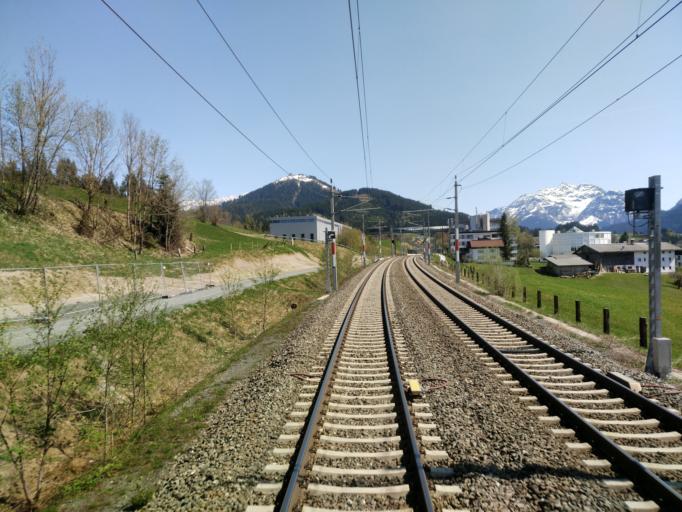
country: AT
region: Tyrol
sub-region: Politischer Bezirk Kitzbuhel
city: Fieberbrunn
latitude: 47.4923
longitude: 12.5251
